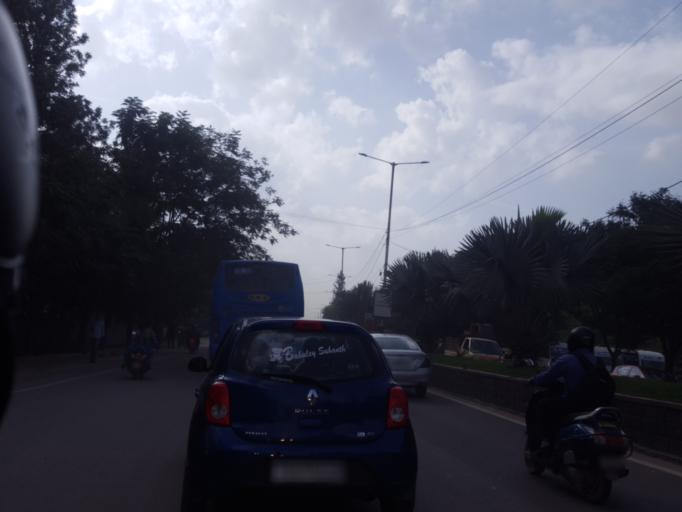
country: IN
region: Telangana
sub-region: Rangareddi
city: Kukatpalli
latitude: 17.4230
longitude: 78.3814
